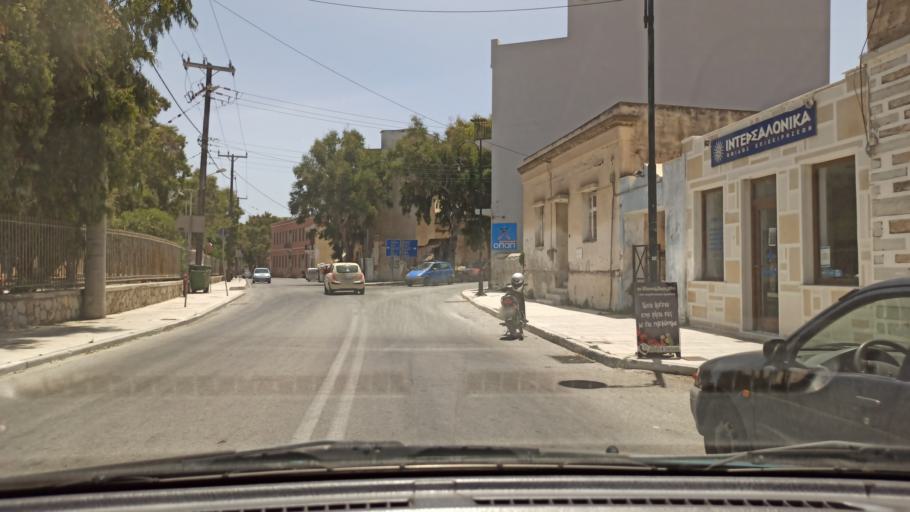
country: GR
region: South Aegean
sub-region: Nomos Kykladon
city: Ermoupolis
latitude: 37.4322
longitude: 24.9349
